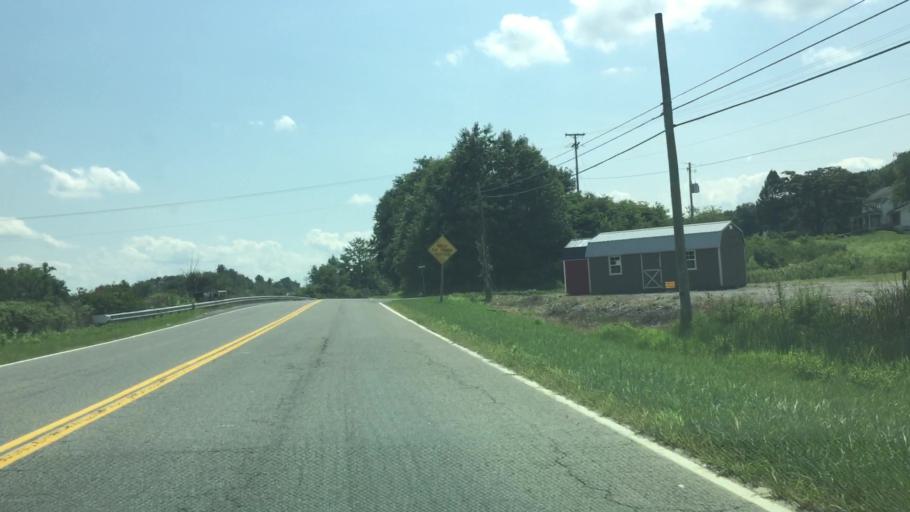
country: US
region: Virginia
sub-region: Pulaski County
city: Pulaski
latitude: 36.9684
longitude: -80.8499
